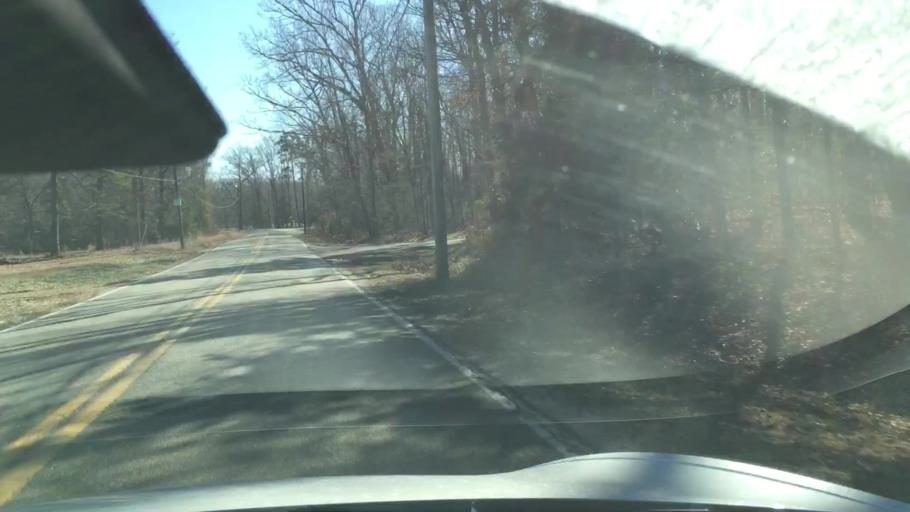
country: US
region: Virginia
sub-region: Henrico County
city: Short Pump
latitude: 37.5889
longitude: -77.7556
